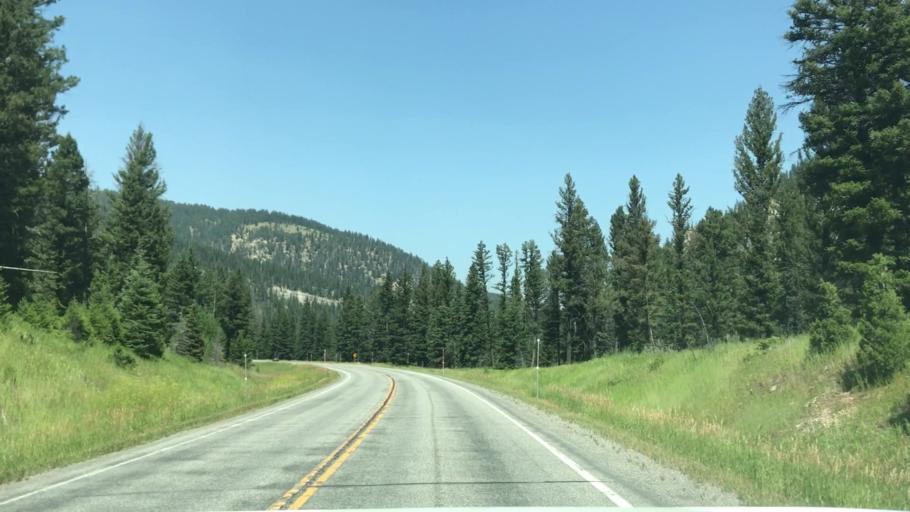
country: US
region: Montana
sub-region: Gallatin County
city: Big Sky
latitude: 45.1547
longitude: -111.2457
